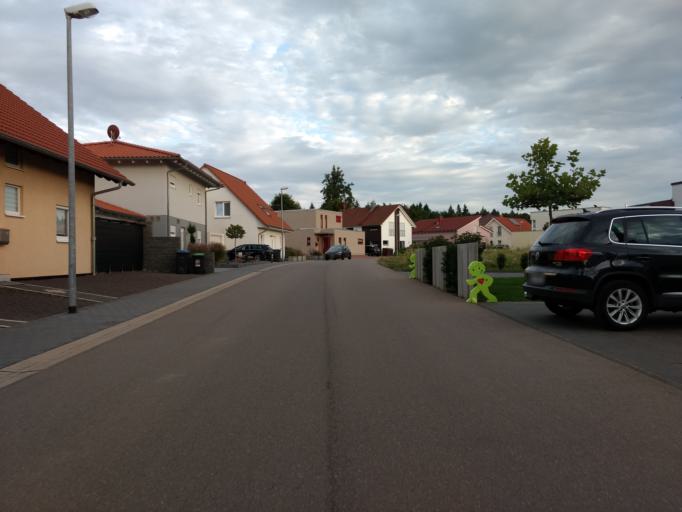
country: DE
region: Saarland
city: Nalbach
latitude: 49.3609
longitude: 6.7829
